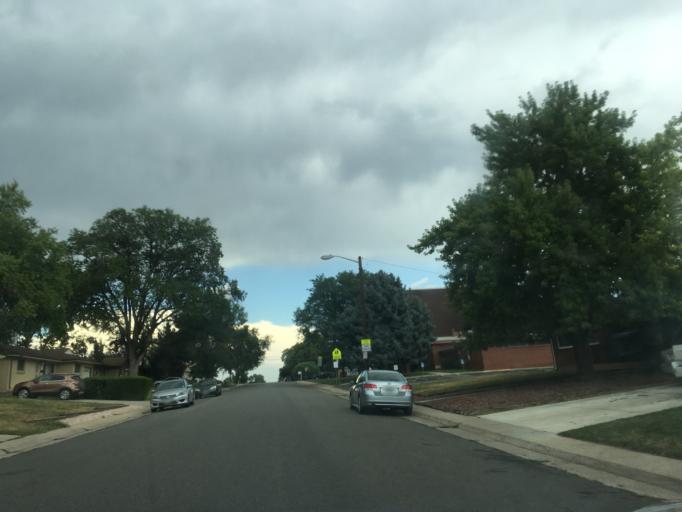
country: US
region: Colorado
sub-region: Arapahoe County
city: Sheridan
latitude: 39.6736
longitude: -105.0387
